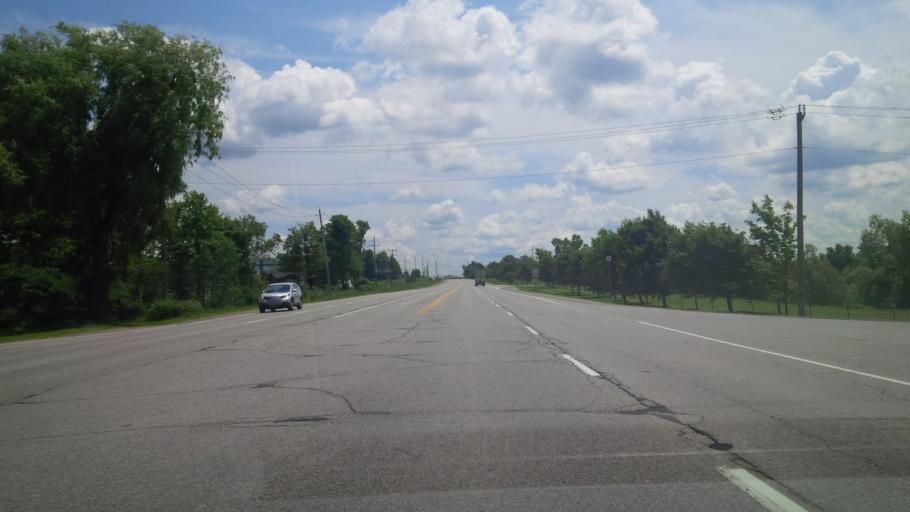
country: CA
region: Ontario
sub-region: Wellington County
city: Guelph
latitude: 43.4668
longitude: -80.1420
